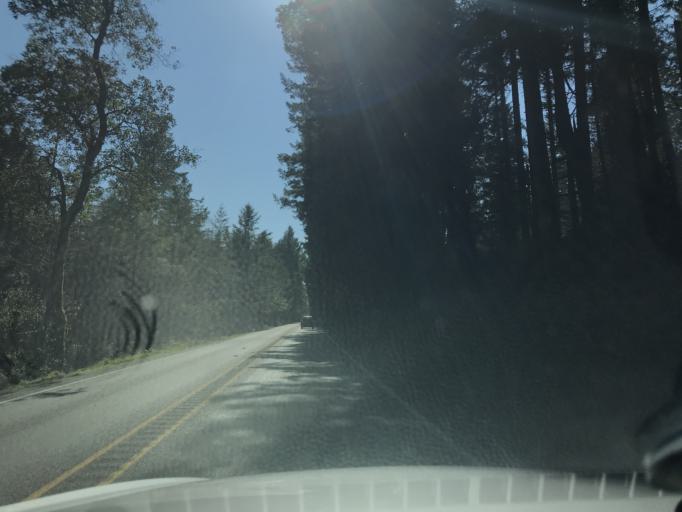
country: US
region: Washington
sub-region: Pierce County
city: Key Center
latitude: 47.3581
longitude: -122.7311
